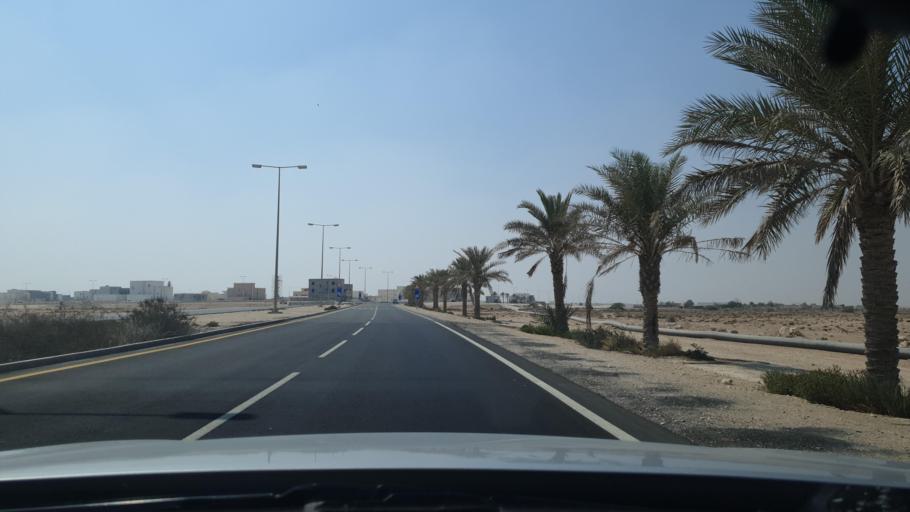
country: QA
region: Al Khawr
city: Al Khawr
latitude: 25.6795
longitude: 51.4775
